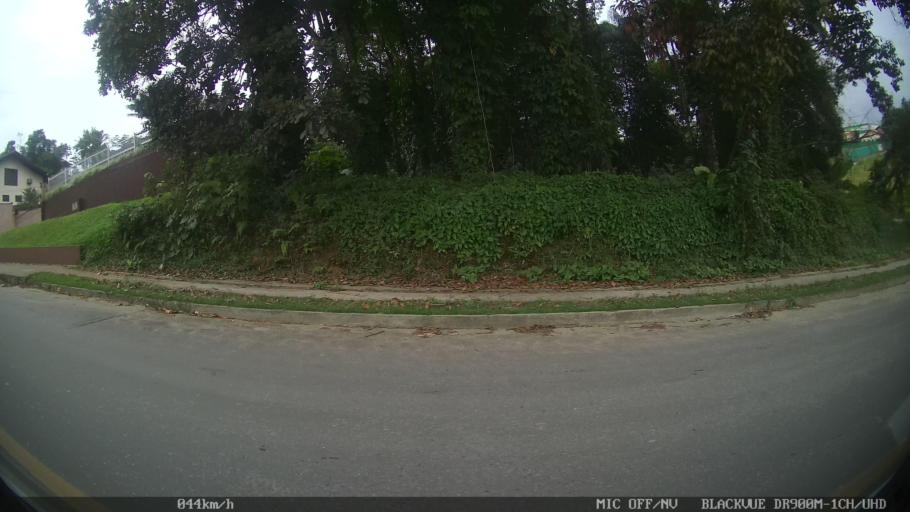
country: BR
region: Santa Catarina
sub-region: Joinville
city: Joinville
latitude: -26.2799
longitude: -48.8787
